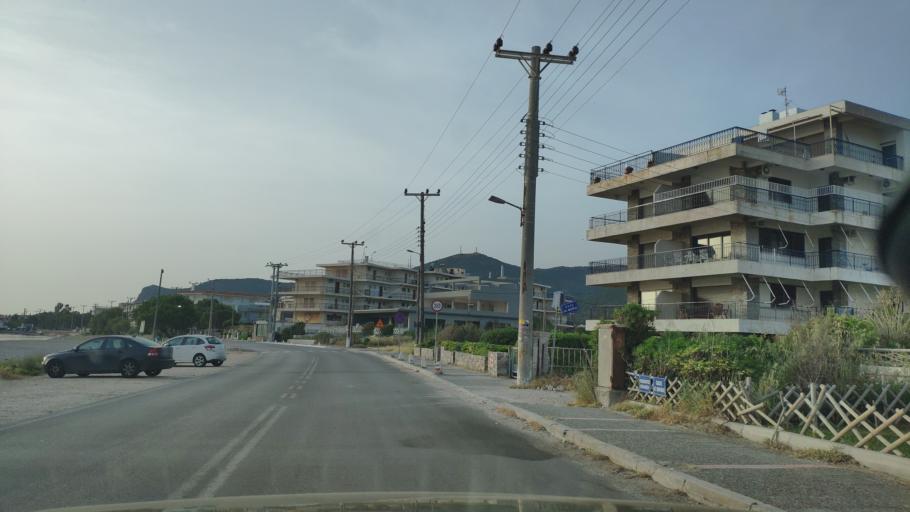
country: GR
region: Attica
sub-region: Nomarchia Anatolikis Attikis
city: Limin Mesoyaias
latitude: 37.8712
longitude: 24.0223
